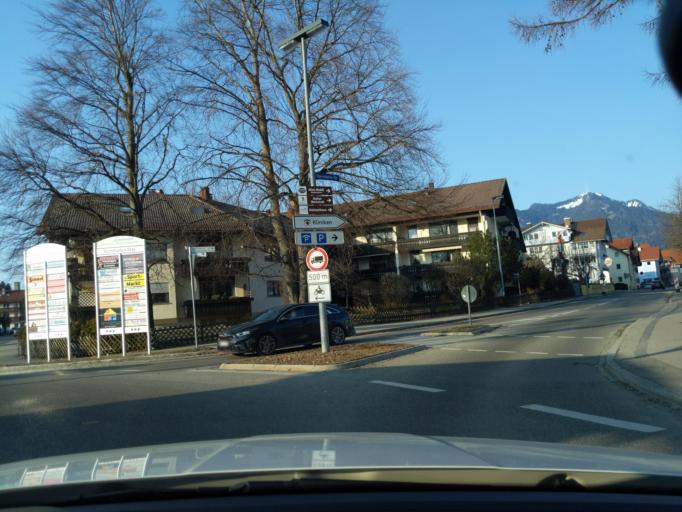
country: DE
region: Bavaria
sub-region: Swabia
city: Sonthofen
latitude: 47.5087
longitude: 10.2764
